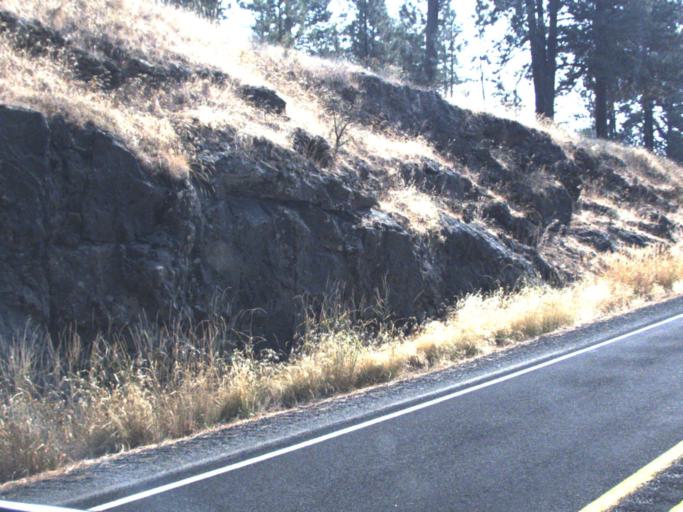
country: US
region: Washington
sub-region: Whitman County
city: Pullman
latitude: 46.9324
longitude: -117.0949
